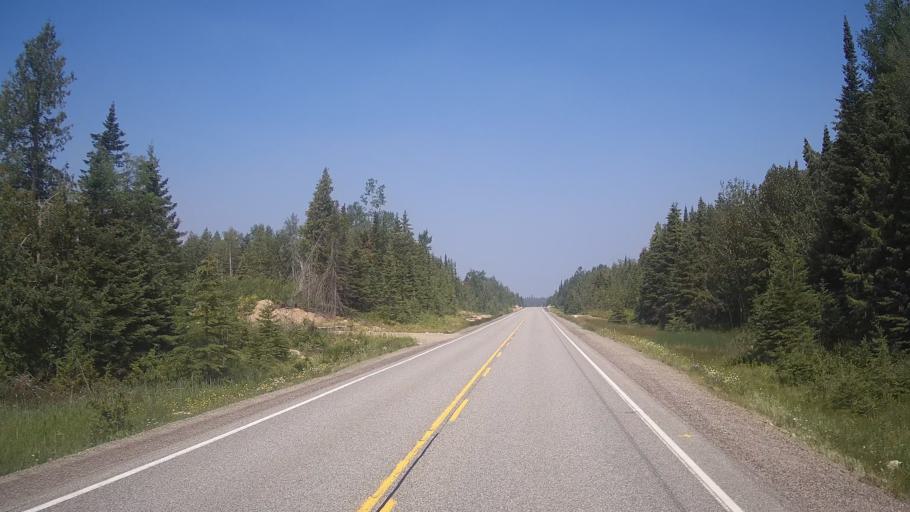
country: CA
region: Ontario
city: Timmins
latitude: 48.0619
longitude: -81.5844
